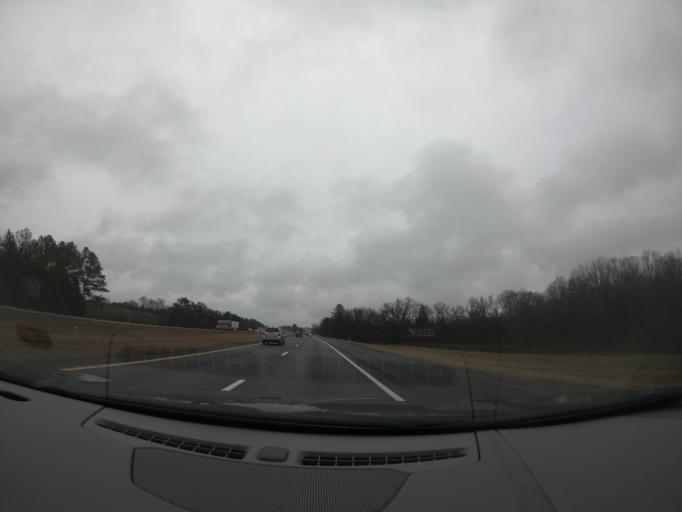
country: US
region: Tennessee
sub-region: Rutherford County
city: Murfreesboro
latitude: 35.7757
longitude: -86.3665
